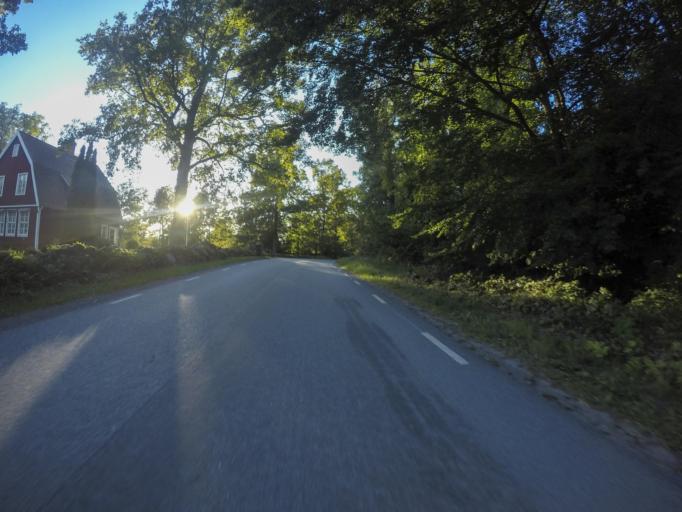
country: SE
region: Vaestmanland
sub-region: Vasteras
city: Vasteras
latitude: 59.5602
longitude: 16.6604
